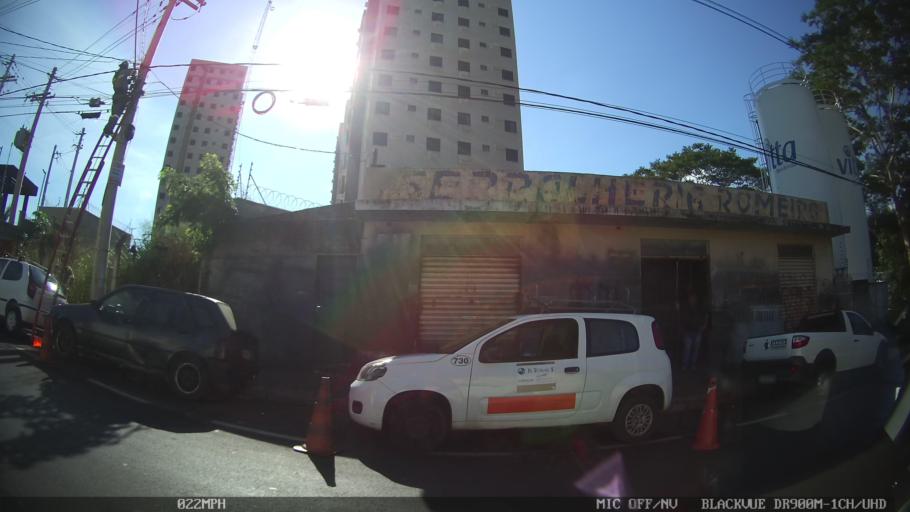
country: BR
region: Sao Paulo
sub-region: Ribeirao Preto
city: Ribeirao Preto
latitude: -21.1702
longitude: -47.7881
